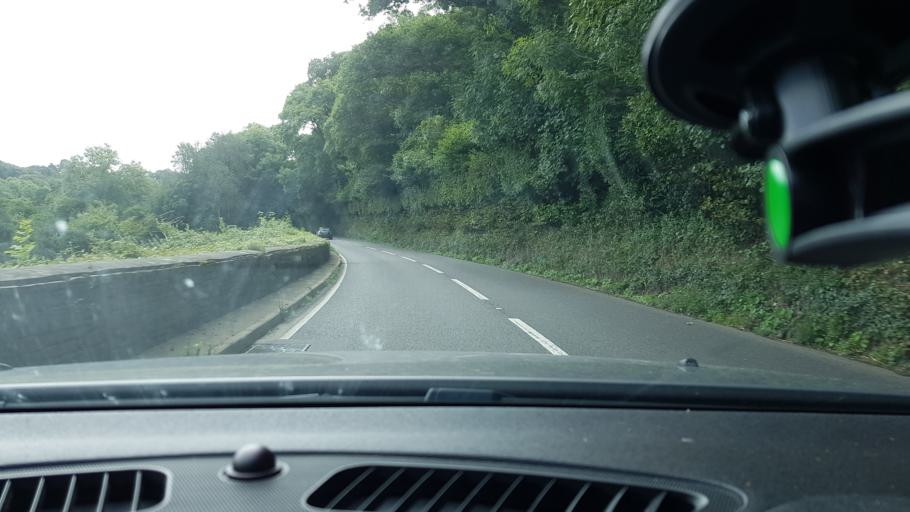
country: GB
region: England
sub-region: Cornwall
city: Camelford
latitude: 50.5741
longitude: -4.7415
